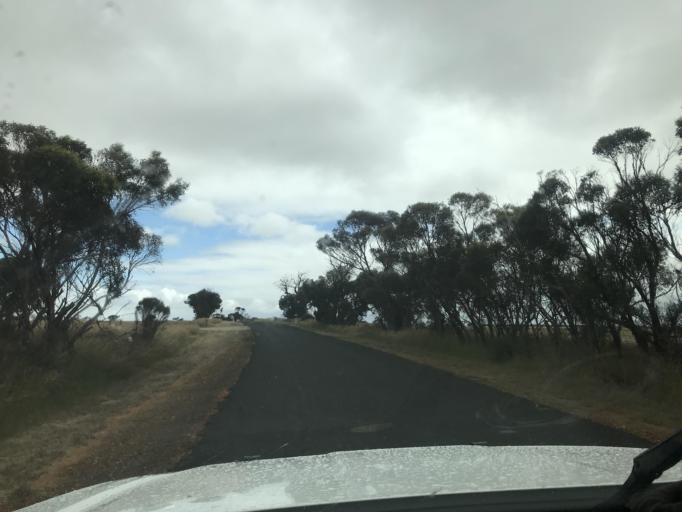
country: AU
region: South Australia
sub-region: Tatiara
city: Bordertown
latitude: -36.2432
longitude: 141.1543
